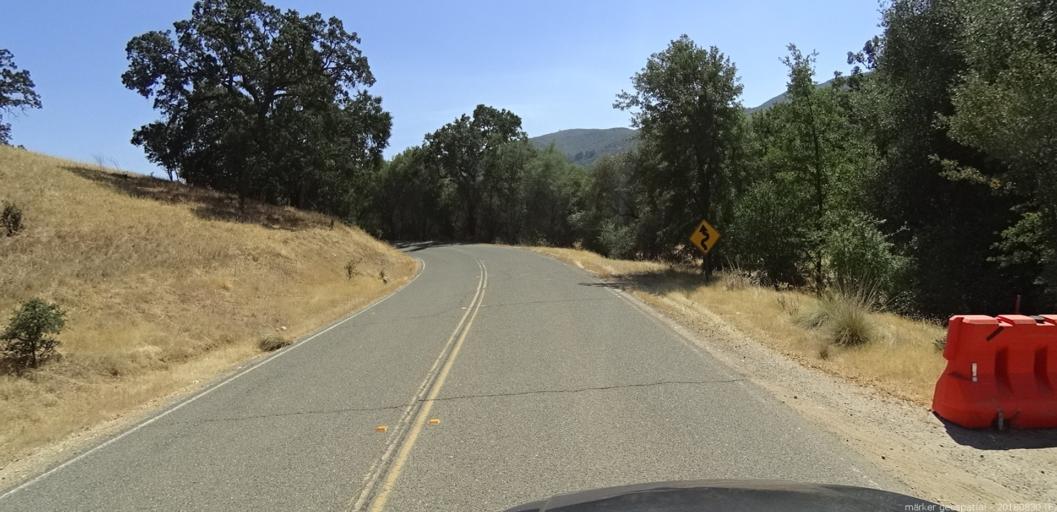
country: US
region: California
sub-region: Monterey County
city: King City
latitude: 35.9783
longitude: -121.3463
